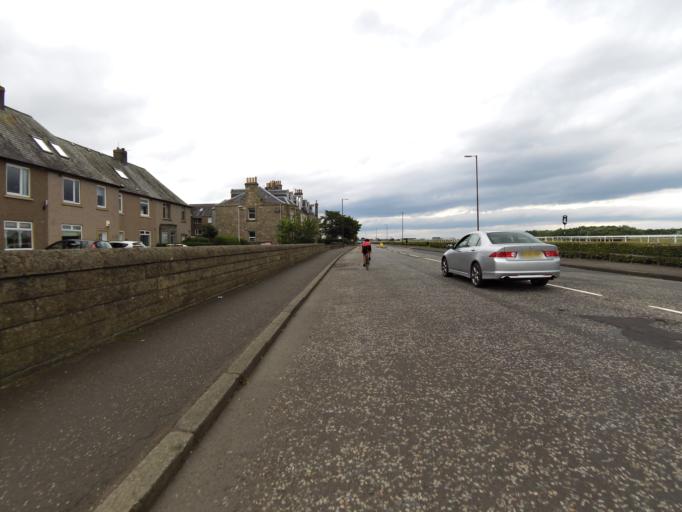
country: GB
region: Scotland
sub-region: East Lothian
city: Musselburgh
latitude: 55.9449
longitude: -3.0312
